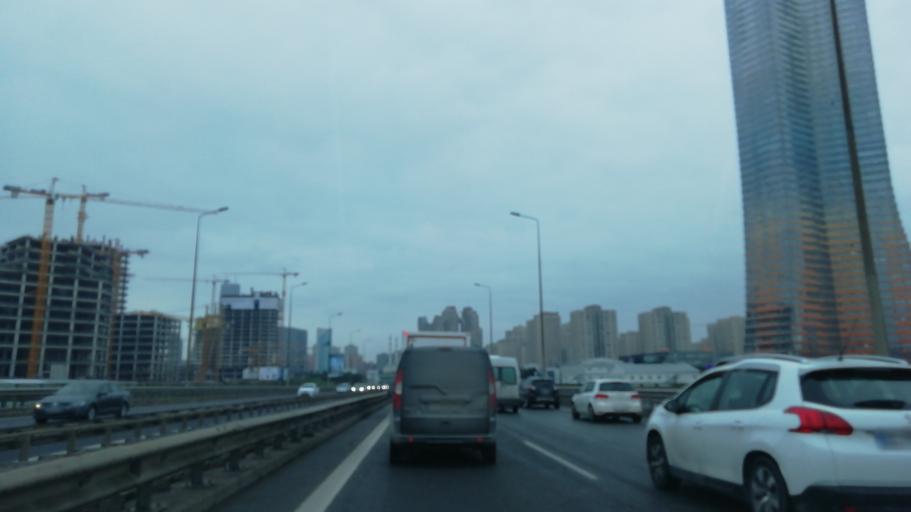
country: TR
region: Istanbul
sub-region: Atasehir
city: Atasehir
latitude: 41.0036
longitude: 29.1024
